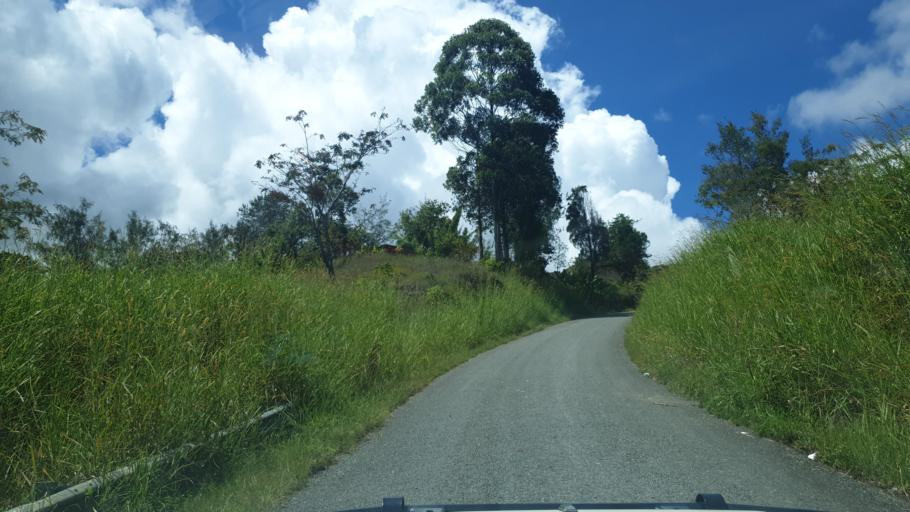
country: PG
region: Chimbu
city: Kundiawa
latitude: -6.1433
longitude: 145.1310
